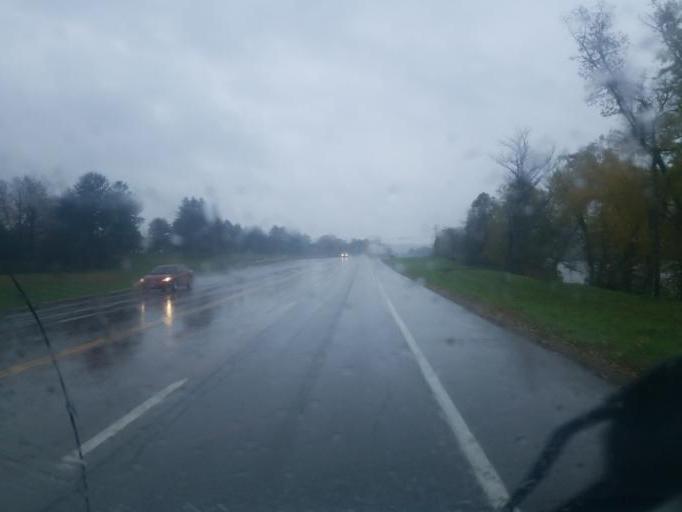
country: US
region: Ohio
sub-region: Muskingum County
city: South Zanesville
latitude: 39.8816
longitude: -81.9807
